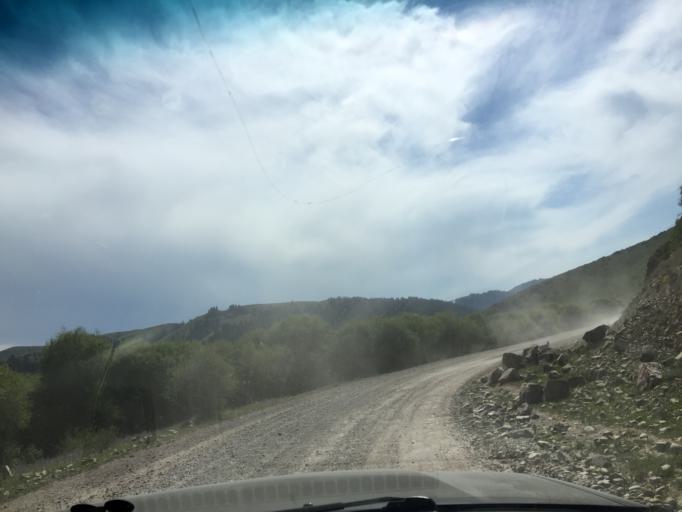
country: KZ
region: Almaty Oblysy
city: Kegen
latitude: 42.7413
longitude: 78.9478
